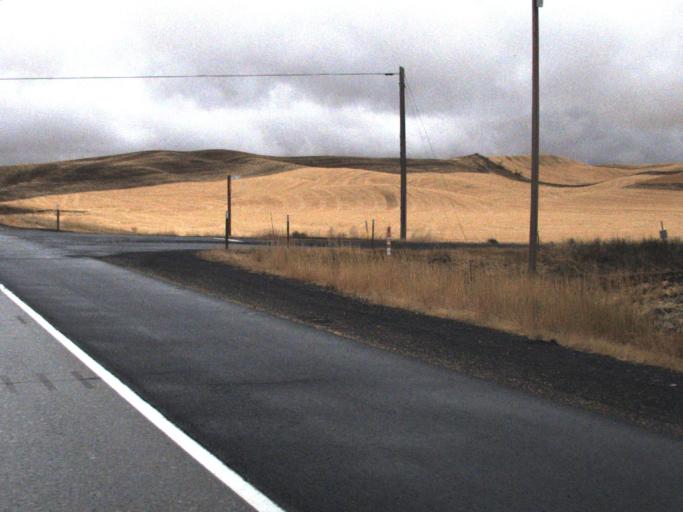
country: US
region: Washington
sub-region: Whitman County
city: Colfax
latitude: 47.0583
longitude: -117.3812
